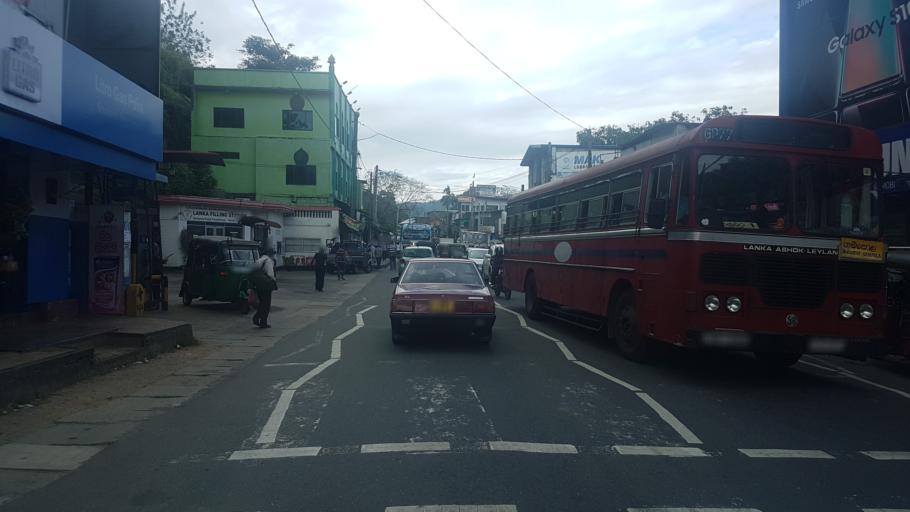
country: LK
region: Central
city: Kandy
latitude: 7.2634
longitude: 80.5930
